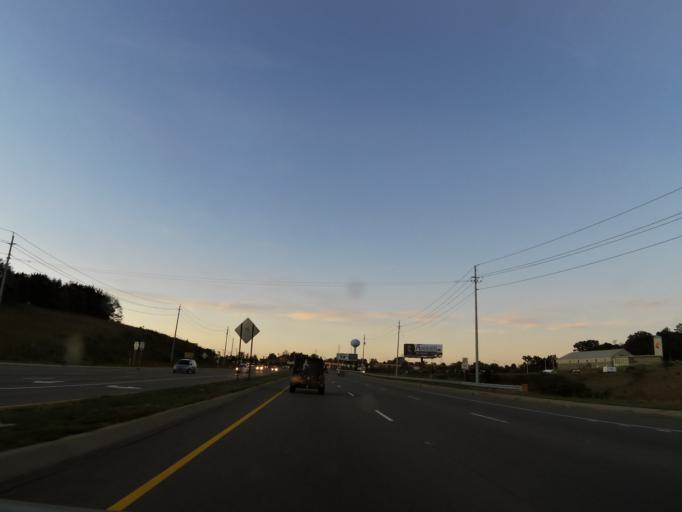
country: US
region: Tennessee
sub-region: Sevier County
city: Sevierville
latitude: 35.9583
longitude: -83.5938
